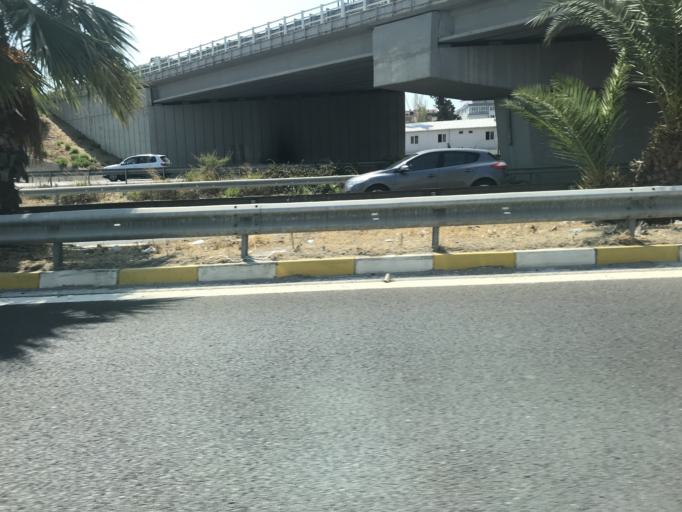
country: TR
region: Izmir
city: Karsiyaka
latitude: 38.3968
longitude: 27.0588
